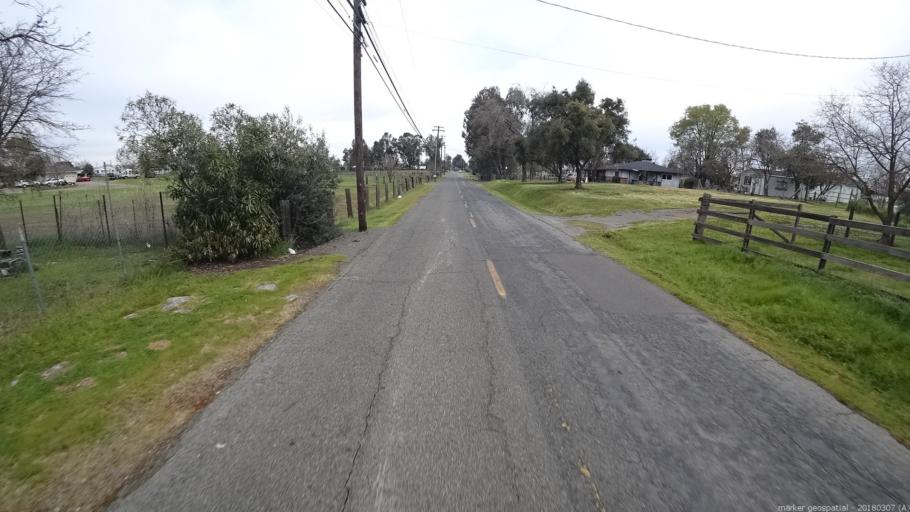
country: US
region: California
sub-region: Sacramento County
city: Rio Linda
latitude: 38.6957
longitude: -121.4661
